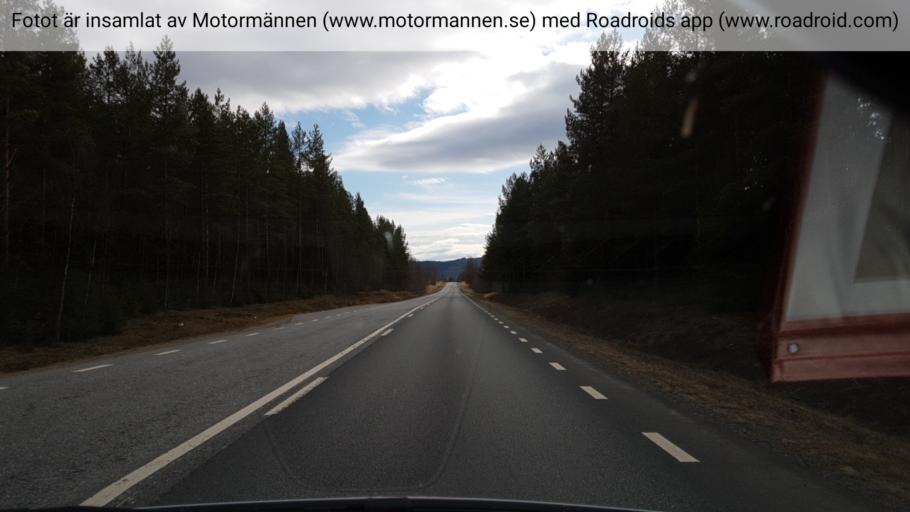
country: SE
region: Vaesternorrland
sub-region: Solleftea Kommun
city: Solleftea
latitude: 63.2550
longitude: 17.2179
